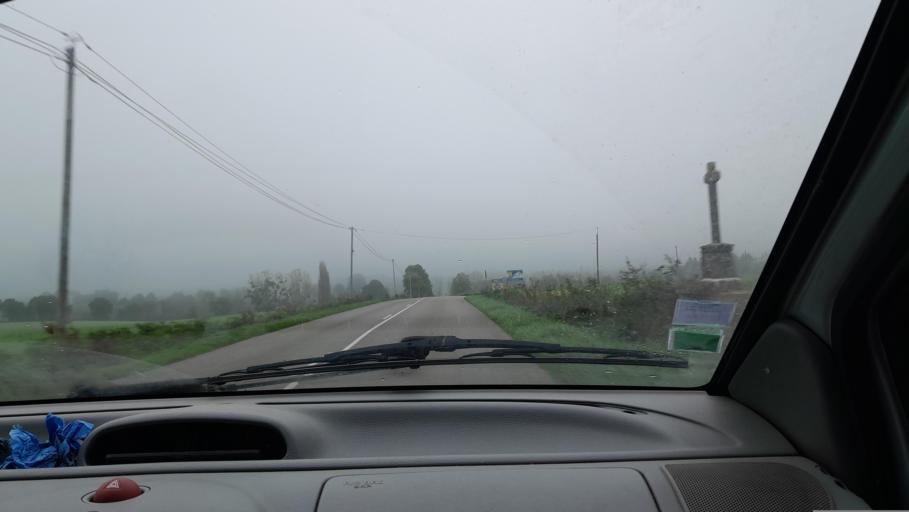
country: FR
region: Brittany
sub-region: Departement d'Ille-et-Vilaine
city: Le Pertre
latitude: 47.9927
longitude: -0.9862
